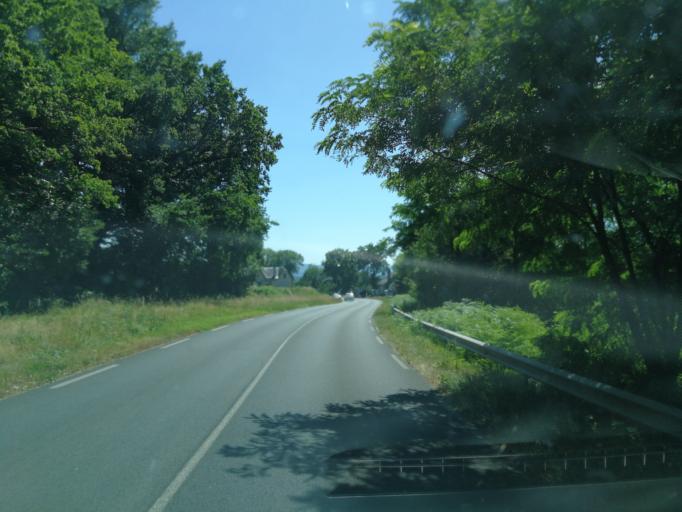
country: FR
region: Limousin
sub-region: Departement de la Correze
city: Sainte-Fereole
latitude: 45.2083
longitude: 1.5844
